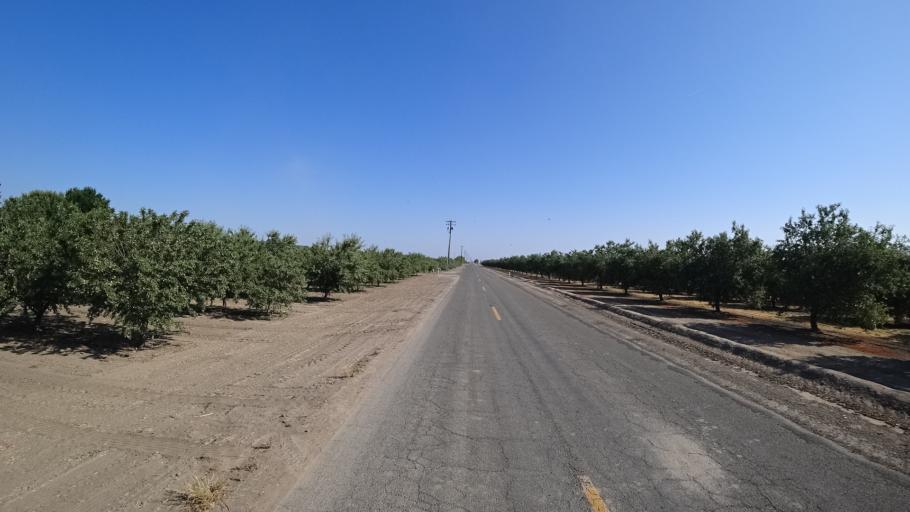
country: US
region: California
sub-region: Kings County
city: Home Garden
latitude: 36.2226
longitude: -119.5831
